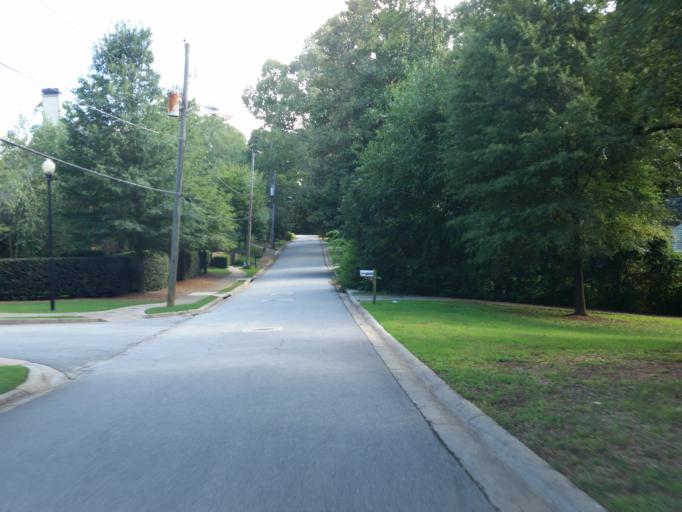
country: US
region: Georgia
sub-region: Cobb County
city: Smyrna
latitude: 33.8883
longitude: -84.5143
